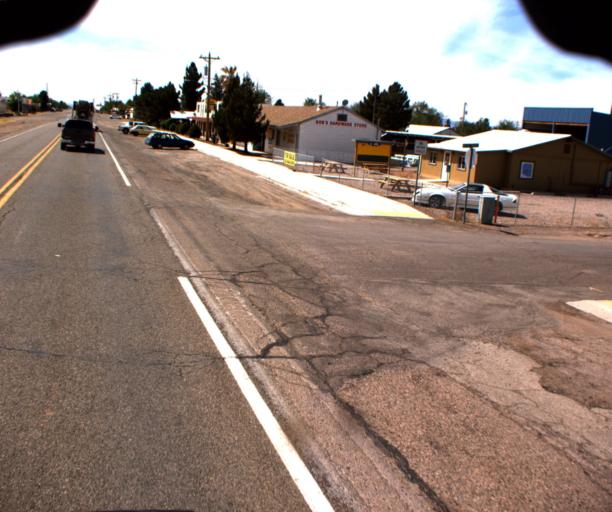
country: US
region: Arizona
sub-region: Cochise County
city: Bisbee
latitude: 31.6870
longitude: -109.6874
